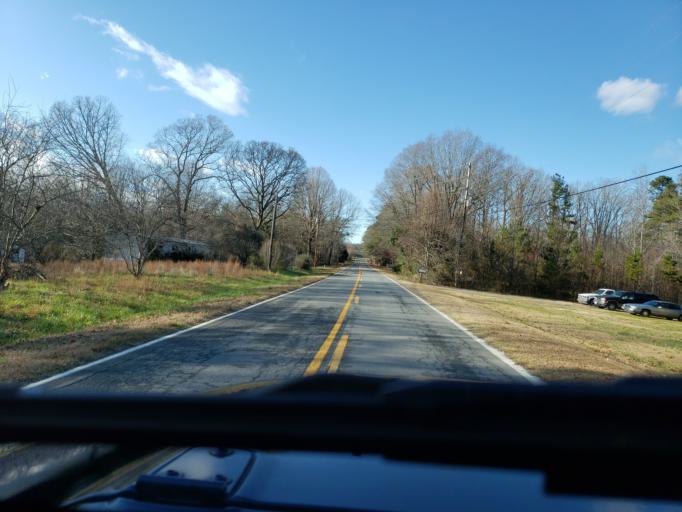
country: US
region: North Carolina
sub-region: Cleveland County
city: Kings Mountain
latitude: 35.1642
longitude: -81.3493
